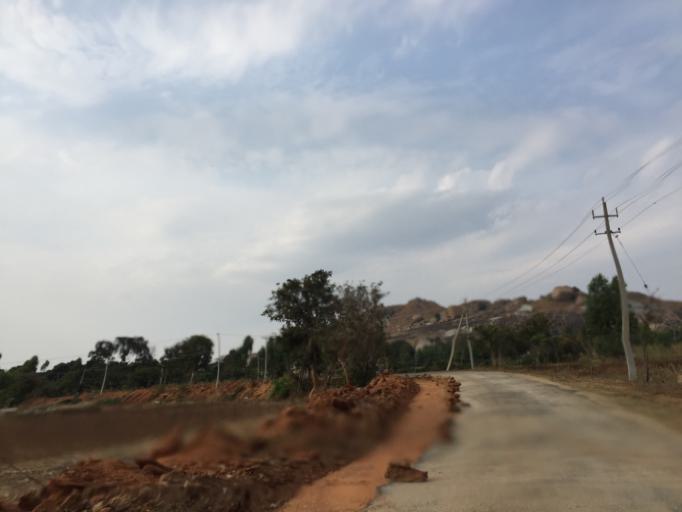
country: IN
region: Karnataka
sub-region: Chikkaballapur
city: Gudibanda
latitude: 13.5755
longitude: 77.7253
